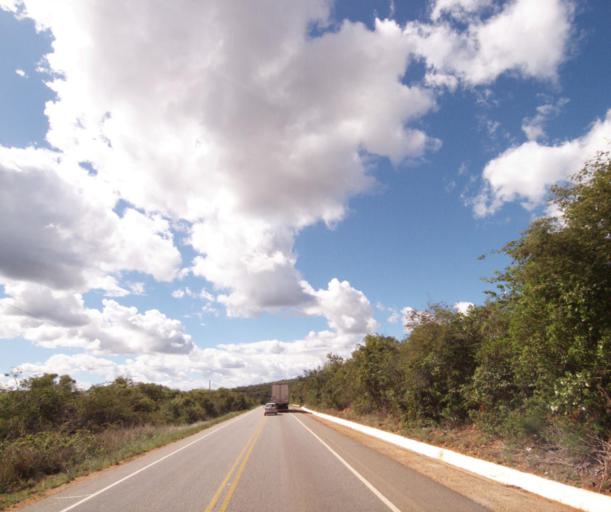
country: BR
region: Bahia
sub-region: Caetite
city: Caetite
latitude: -14.1421
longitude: -42.3788
